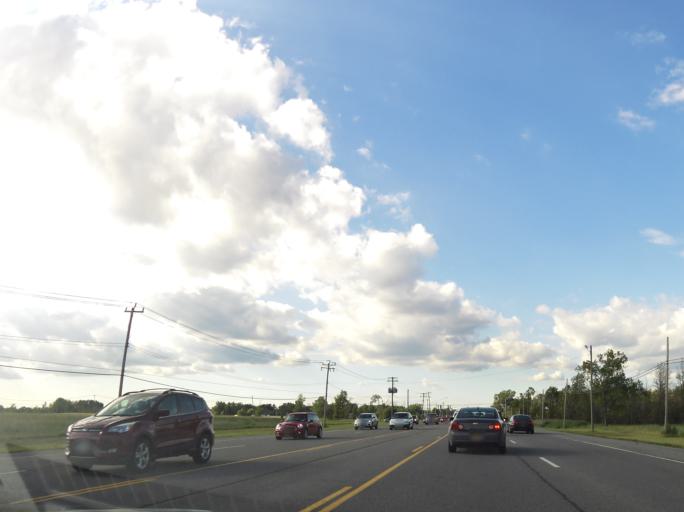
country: US
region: New York
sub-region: Erie County
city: Harris Hill
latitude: 42.9429
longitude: -78.6967
